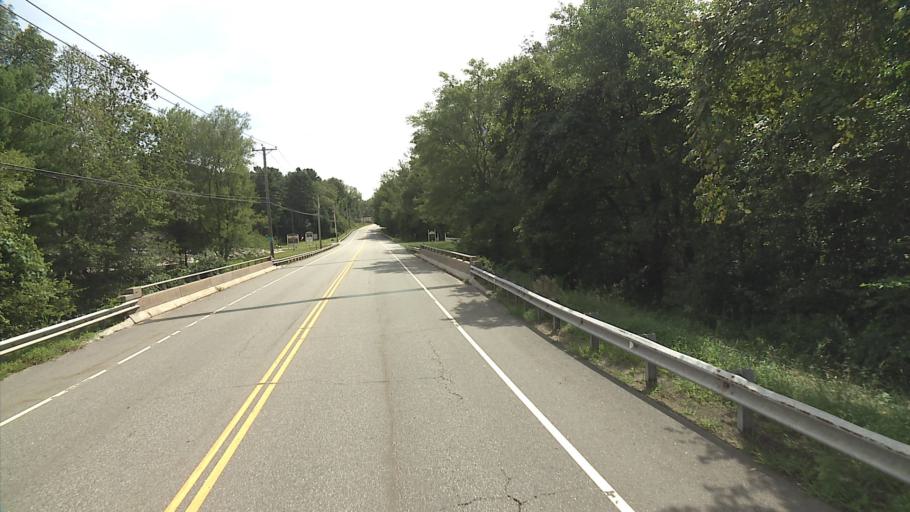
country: US
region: Connecticut
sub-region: Windham County
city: South Woodstock
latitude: 41.9336
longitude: -71.9381
